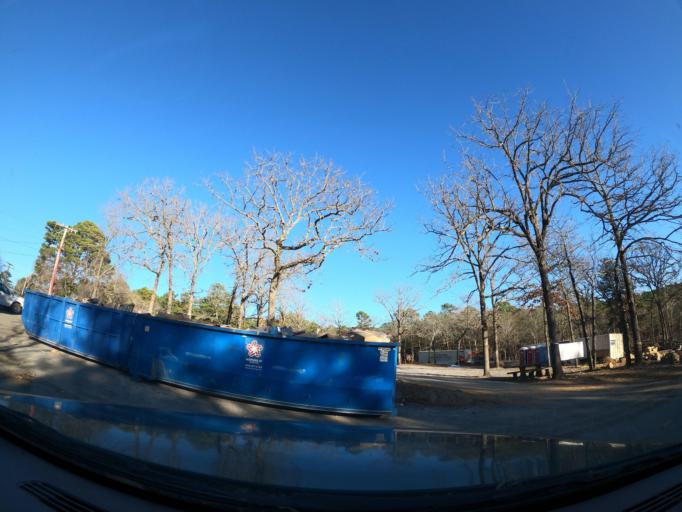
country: US
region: Oklahoma
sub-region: Latimer County
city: Wilburton
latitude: 34.9798
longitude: -95.3606
